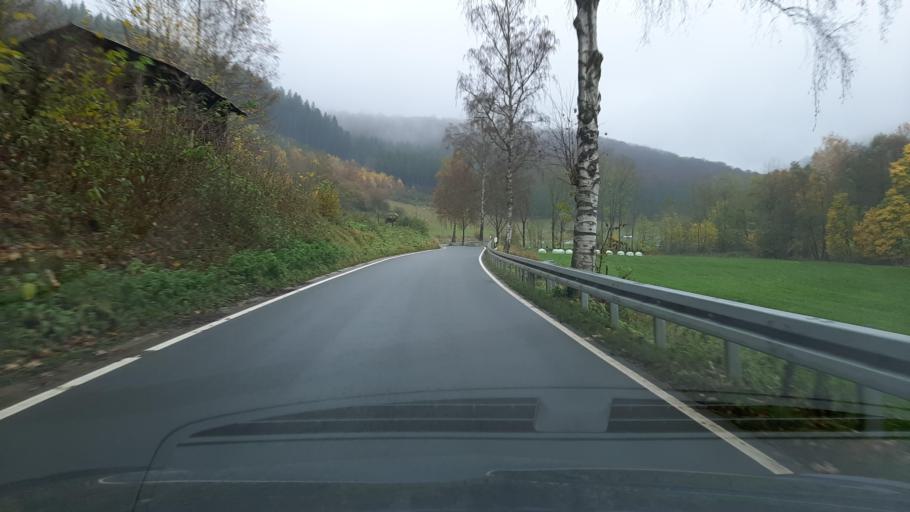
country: DE
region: North Rhine-Westphalia
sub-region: Regierungsbezirk Arnsberg
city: Bad Fredeburg
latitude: 51.1736
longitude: 8.3651
